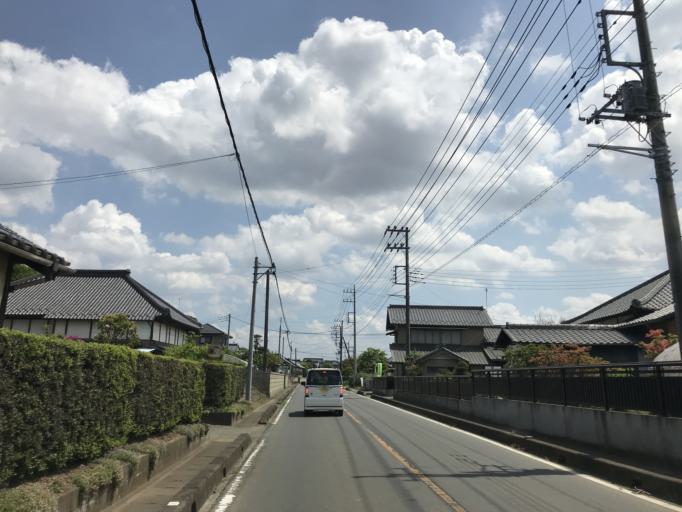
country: JP
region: Ibaraki
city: Mitsukaido
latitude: 36.0530
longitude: 140.0386
